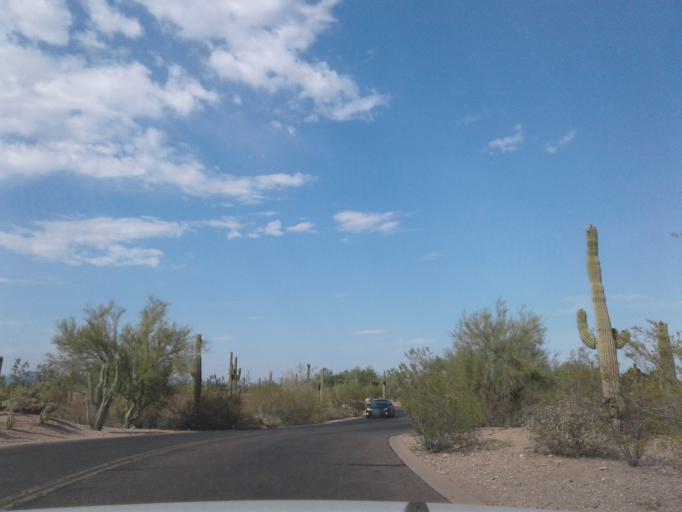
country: US
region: Arizona
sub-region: Maricopa County
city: Tempe Junction
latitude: 33.4614
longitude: -111.9482
